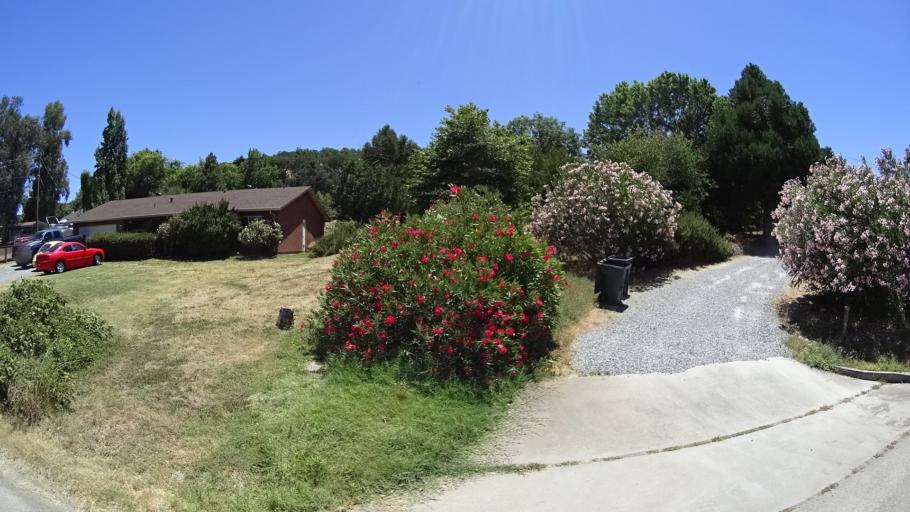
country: US
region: California
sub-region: Calaveras County
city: Rancho Calaveras
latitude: 38.1552
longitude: -120.8505
